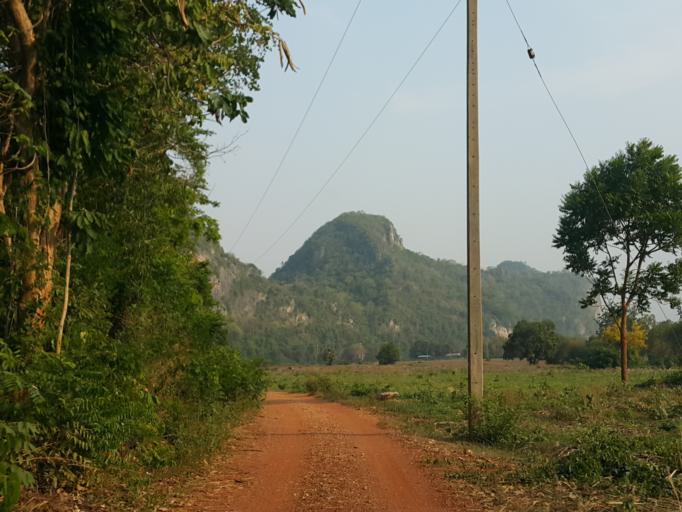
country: TH
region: Uthai Thani
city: Huai Khot
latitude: 15.3286
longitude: 99.6757
